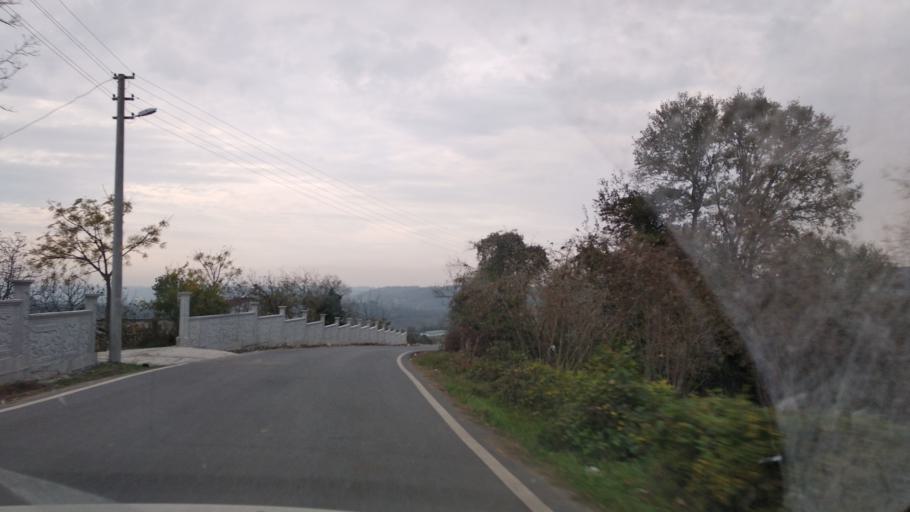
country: TR
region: Sakarya
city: Ortakoy
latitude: 41.0384
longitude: 30.6542
